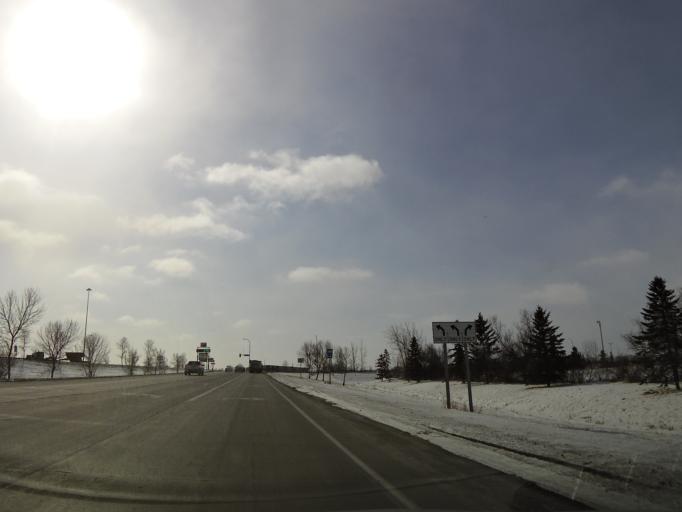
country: US
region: North Dakota
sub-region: Grand Forks County
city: Grand Forks
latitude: 47.8911
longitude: -97.0899
